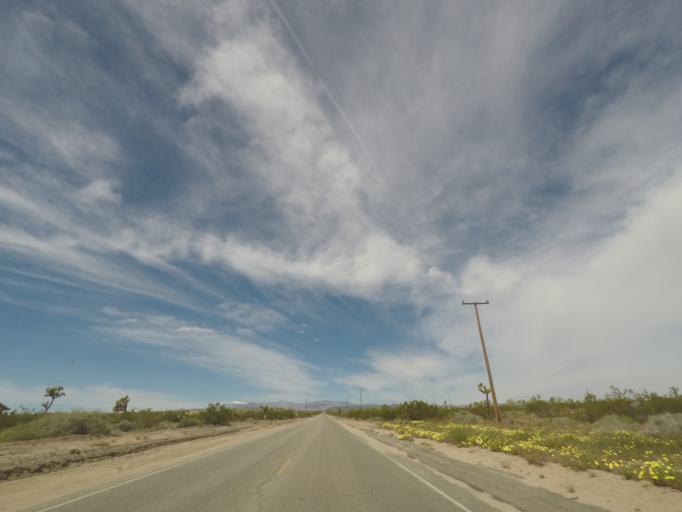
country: US
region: California
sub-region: San Bernardino County
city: Joshua Tree
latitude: 34.1931
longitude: -116.3526
